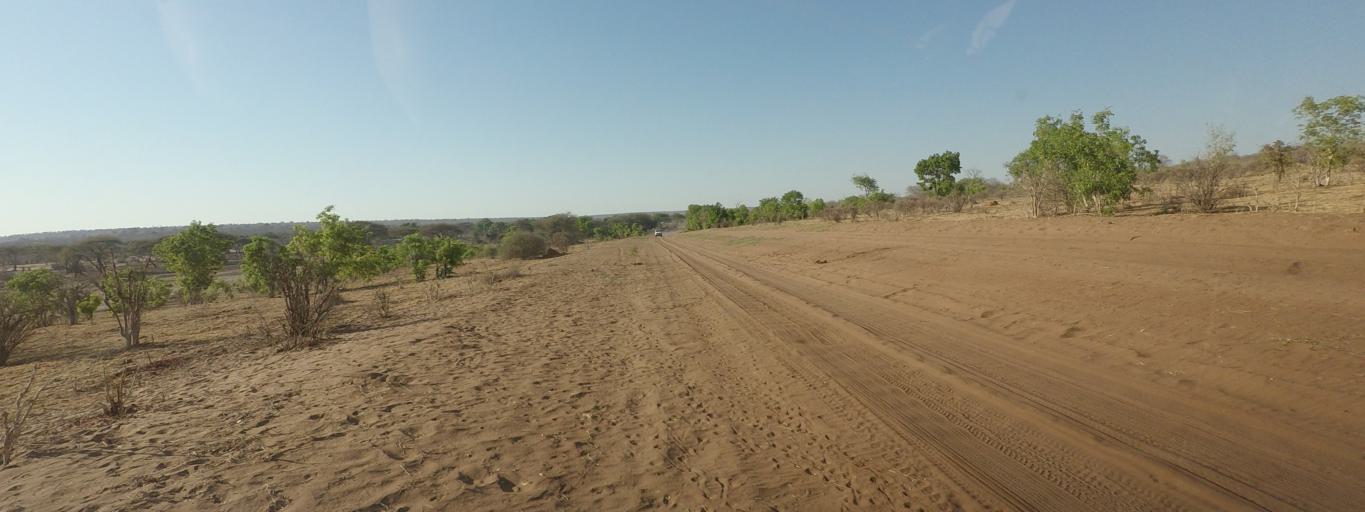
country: BW
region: North West
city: Kasane
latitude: -17.8761
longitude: 25.2344
